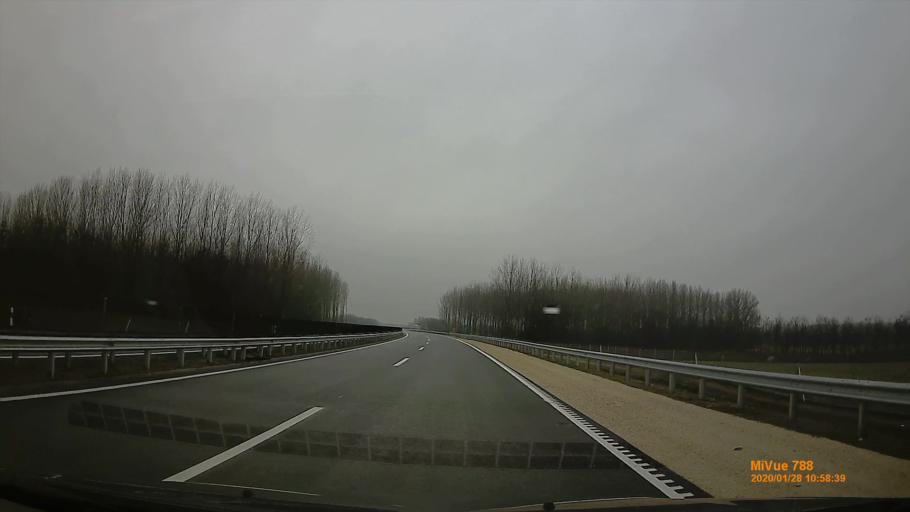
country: HU
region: Pest
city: Peteri
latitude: 47.3782
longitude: 19.3962
